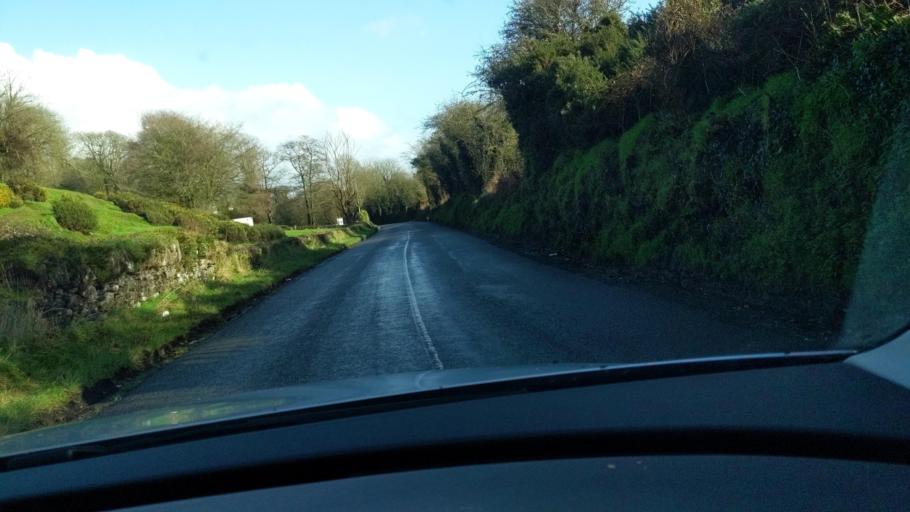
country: IE
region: Munster
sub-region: County Cork
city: Cork
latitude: 51.9266
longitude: -8.5015
